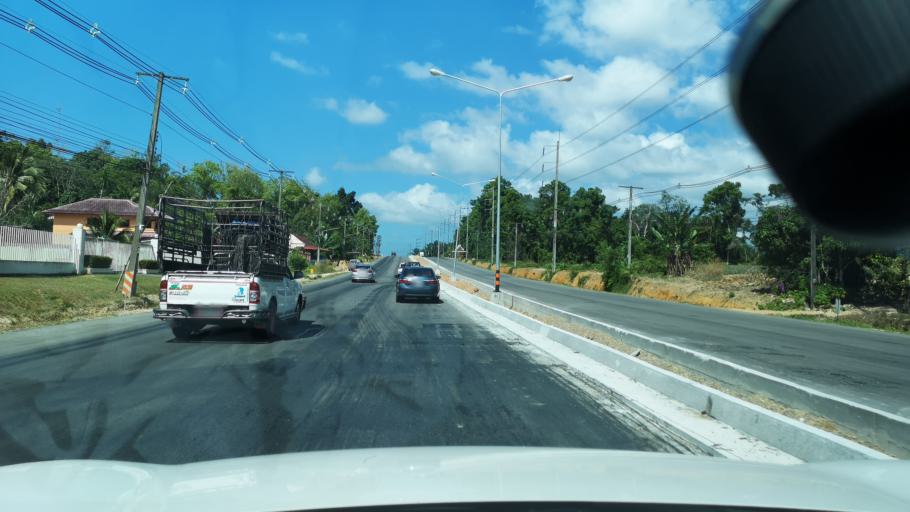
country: TH
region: Phangnga
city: Thai Mueang
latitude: 8.4268
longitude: 98.2584
